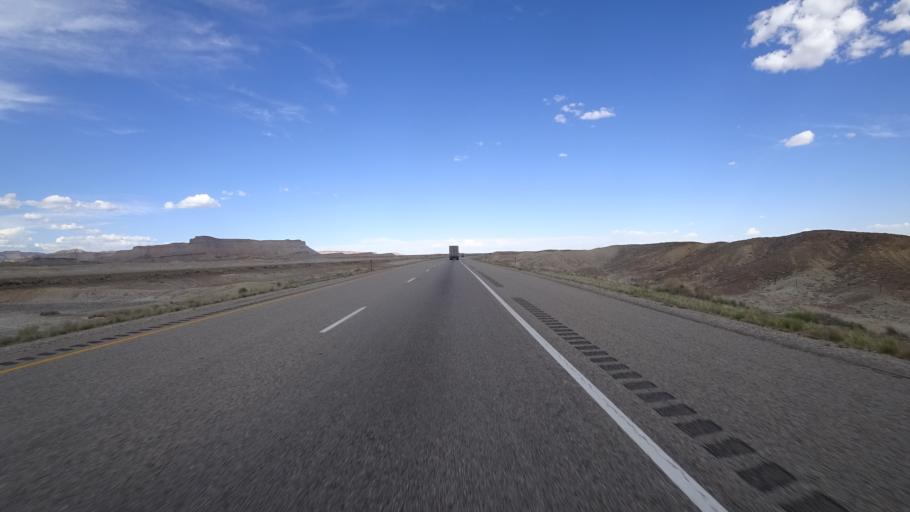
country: US
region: Utah
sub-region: Grand County
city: Moab
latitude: 38.9259
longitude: -109.9932
